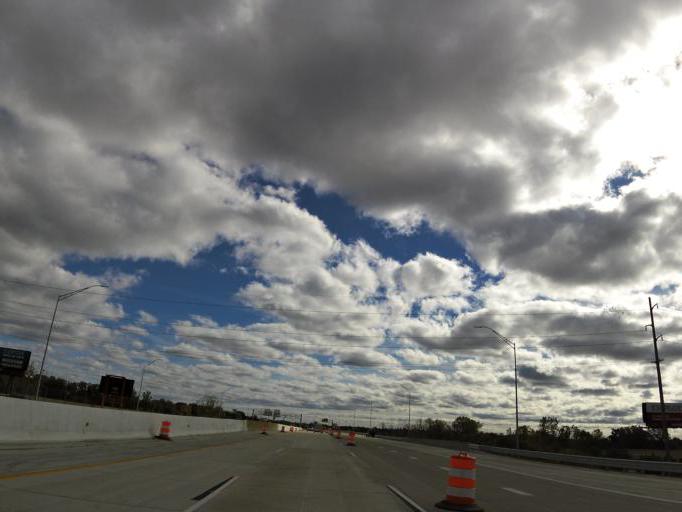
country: US
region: Michigan
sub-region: Genesee County
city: Burton
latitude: 43.0123
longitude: -83.6507
